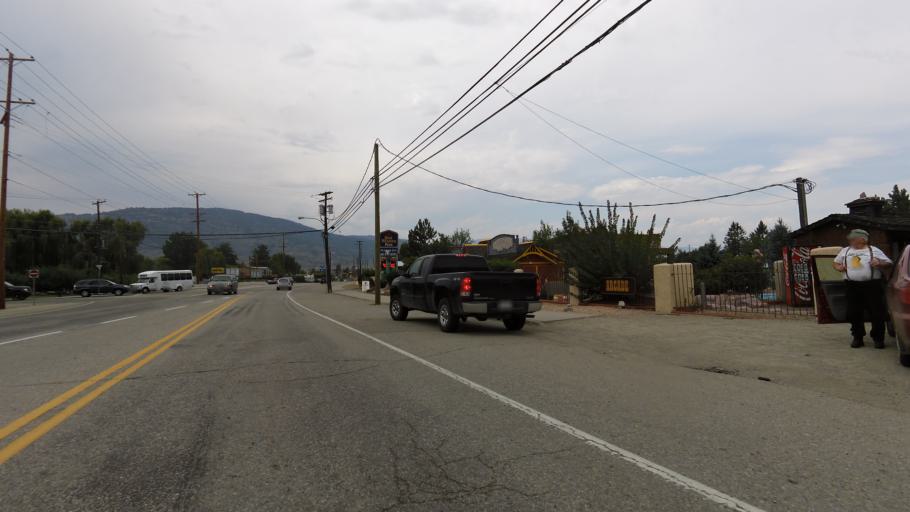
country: CA
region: British Columbia
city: Osoyoos
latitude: 49.0281
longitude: -119.4418
